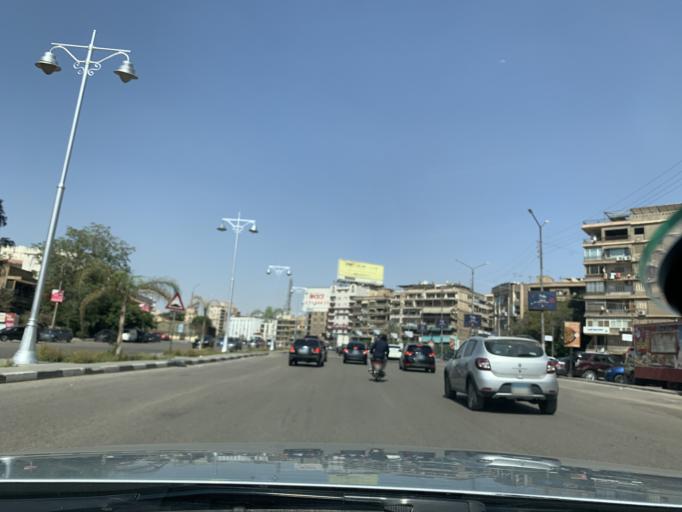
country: EG
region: Muhafazat al Qahirah
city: Cairo
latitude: 30.0848
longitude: 31.3310
